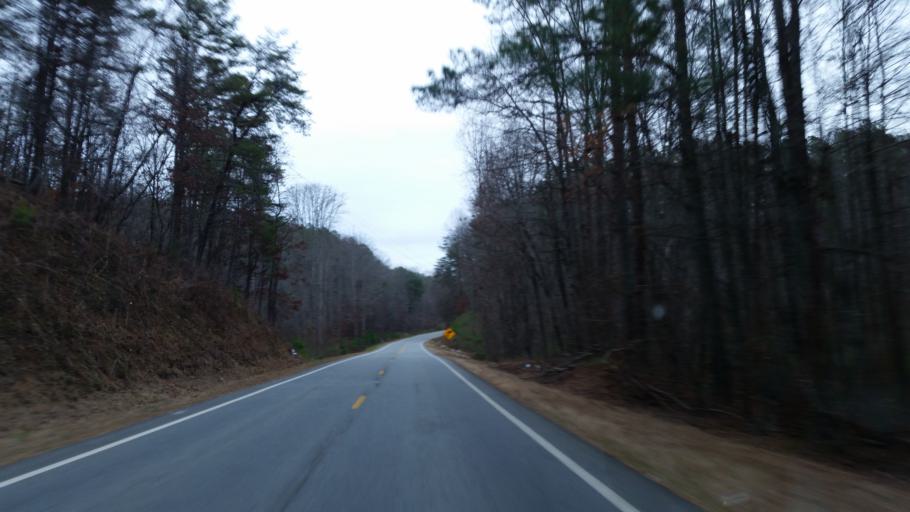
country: US
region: Georgia
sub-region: Dawson County
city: Dawsonville
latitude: 34.4511
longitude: -84.1231
